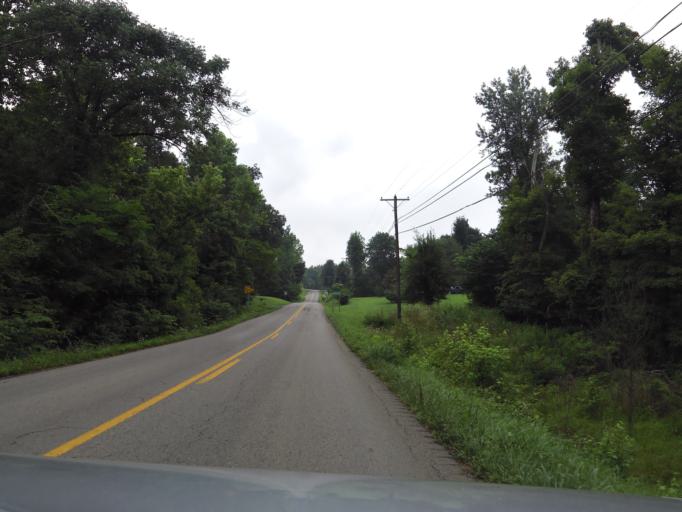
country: US
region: Kentucky
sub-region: Muhlenberg County
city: Morehead
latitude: 37.2591
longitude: -87.2824
